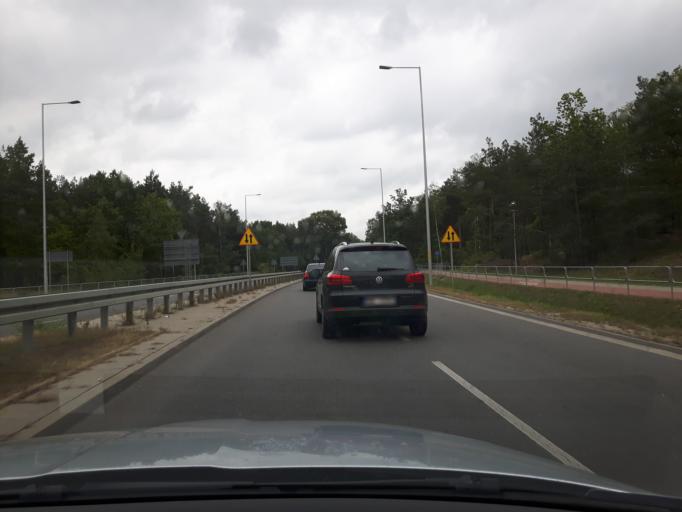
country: PL
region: Masovian Voivodeship
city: Zielonka
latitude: 52.2955
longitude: 21.1410
